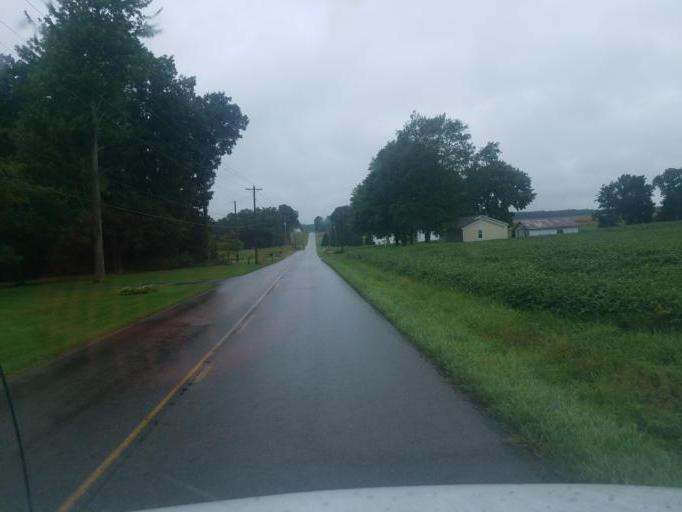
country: US
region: Ohio
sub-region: Medina County
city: Westfield Center
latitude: 40.9737
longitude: -81.9668
